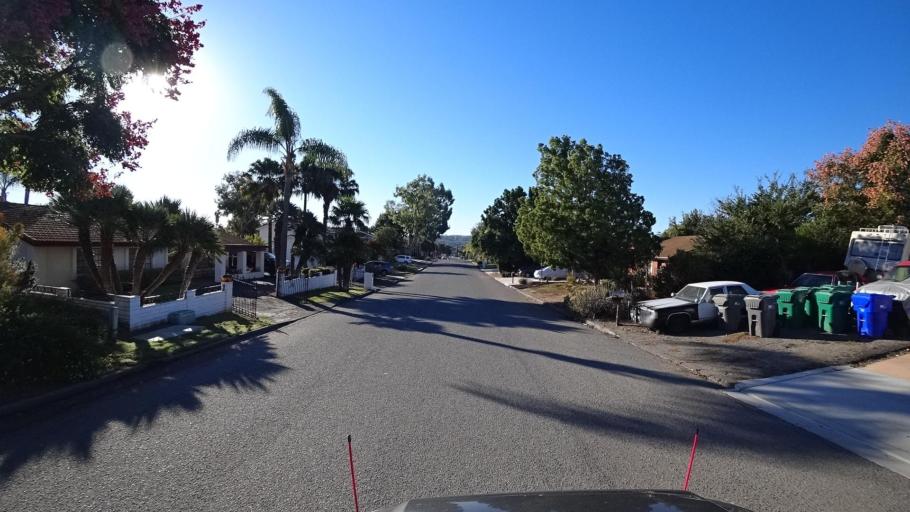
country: US
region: California
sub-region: San Diego County
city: Bonita
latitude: 32.6741
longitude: -117.0305
